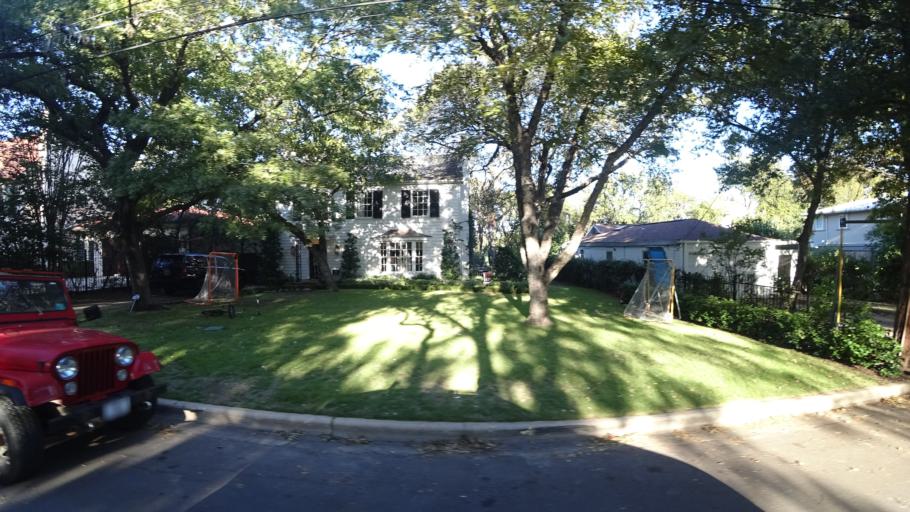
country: US
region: Texas
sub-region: Travis County
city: Austin
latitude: 30.2952
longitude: -97.7501
